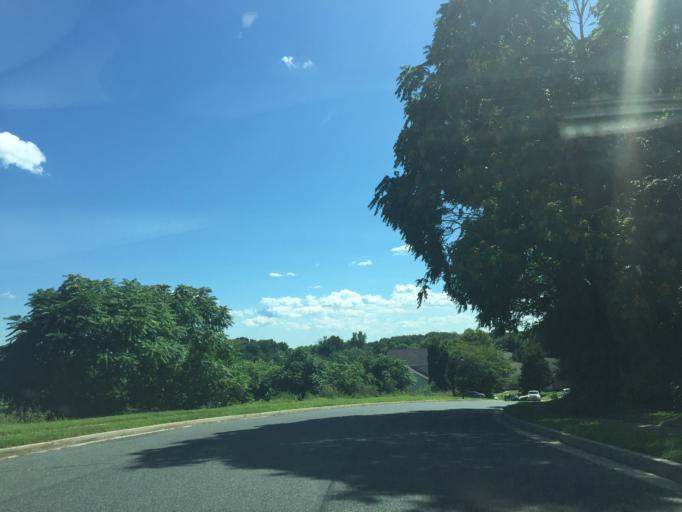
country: US
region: Maryland
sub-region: Baltimore County
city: Perry Hall
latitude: 39.4149
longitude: -76.4838
